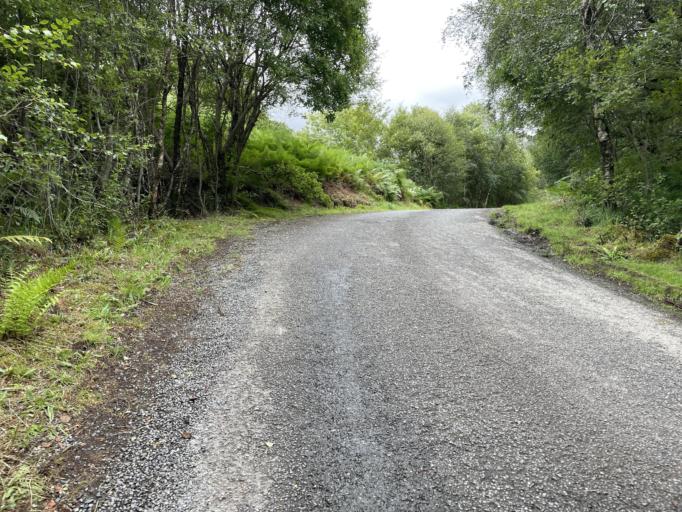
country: GB
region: Scotland
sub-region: Dumfries and Galloway
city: Newton Stewart
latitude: 55.0920
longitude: -4.4859
